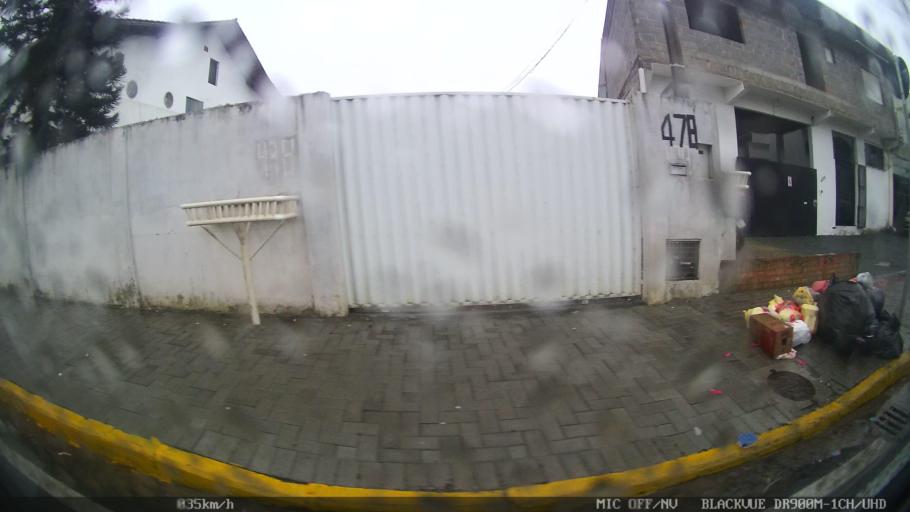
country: BR
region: Santa Catarina
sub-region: Navegantes
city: Navegantes
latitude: -26.8804
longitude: -48.6461
